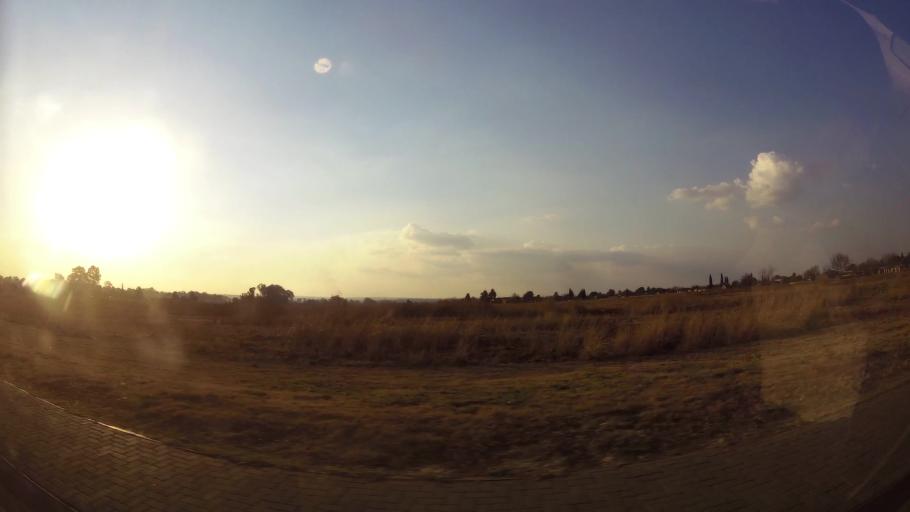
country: ZA
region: Gauteng
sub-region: Ekurhuleni Metropolitan Municipality
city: Germiston
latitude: -26.3077
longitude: 28.2362
